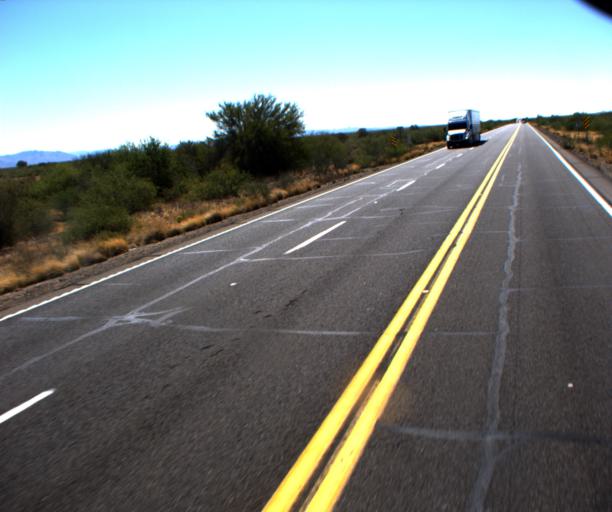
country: US
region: Arizona
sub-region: Yavapai County
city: Congress
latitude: 34.1330
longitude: -112.9643
